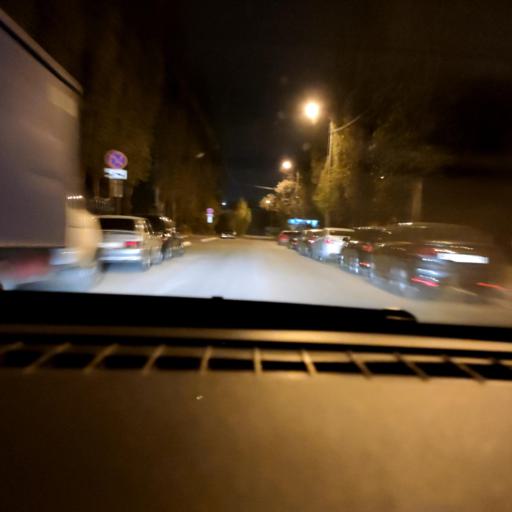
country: RU
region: Voronezj
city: Voronezh
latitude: 51.6905
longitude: 39.1444
